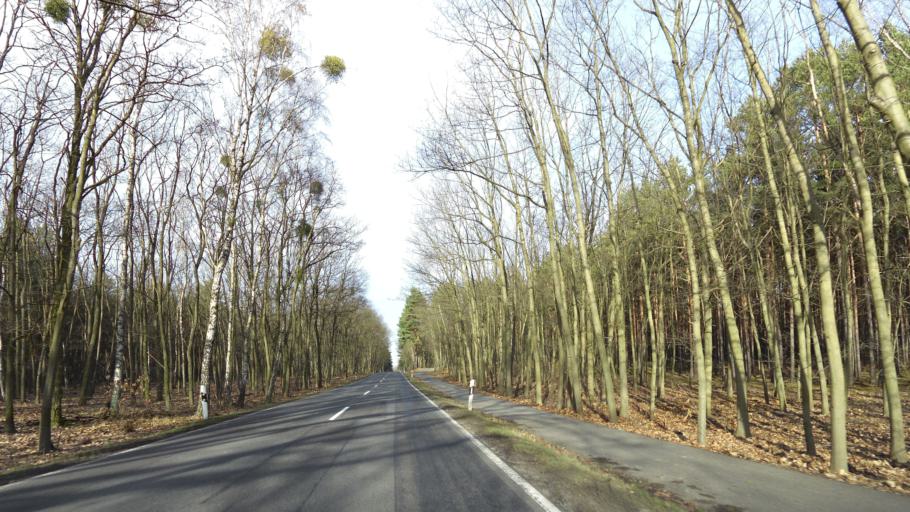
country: DE
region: Brandenburg
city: Michendorf
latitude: 52.3350
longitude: 13.0173
